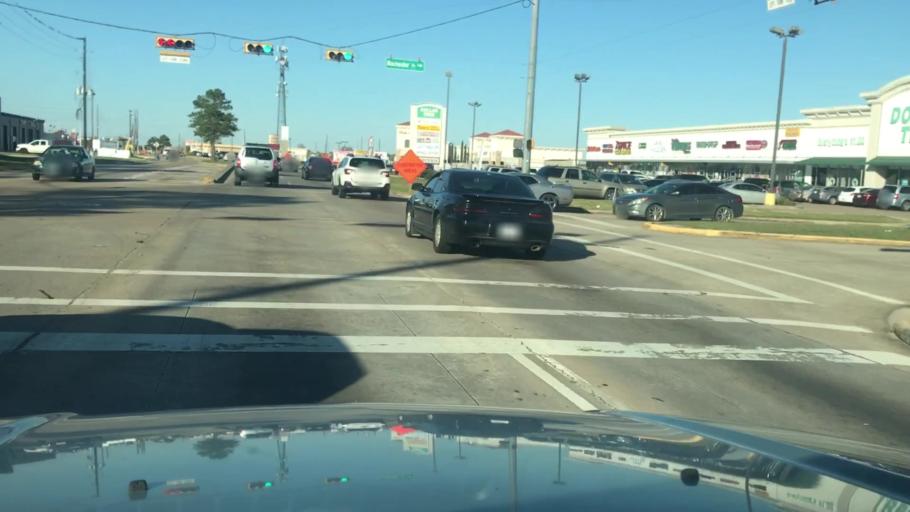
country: US
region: Texas
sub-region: Fort Bend County
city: Cinco Ranch
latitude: 29.8498
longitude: -95.7188
